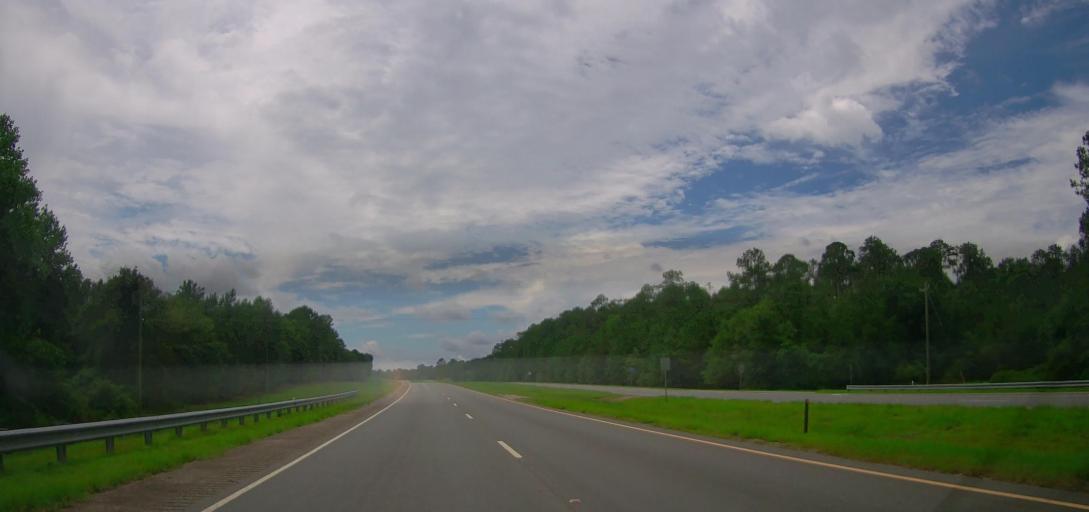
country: US
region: Georgia
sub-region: Telfair County
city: Helena
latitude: 32.1044
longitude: -82.9687
